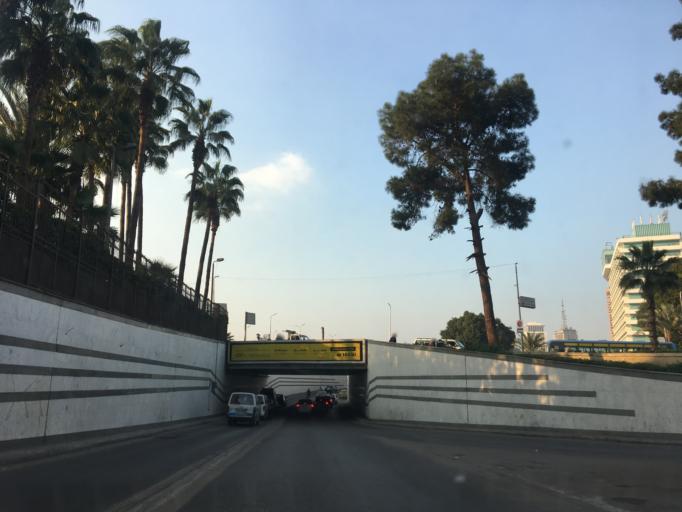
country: EG
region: Muhafazat al Qahirah
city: Cairo
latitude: 30.0435
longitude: 31.2324
